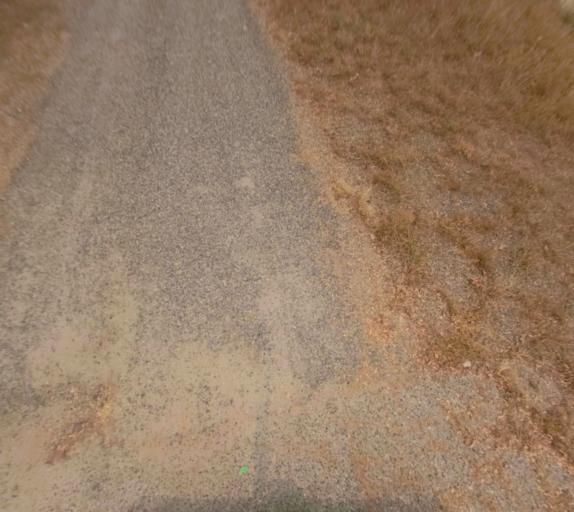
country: US
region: California
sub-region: Madera County
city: Oakhurst
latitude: 37.3418
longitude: -119.6413
